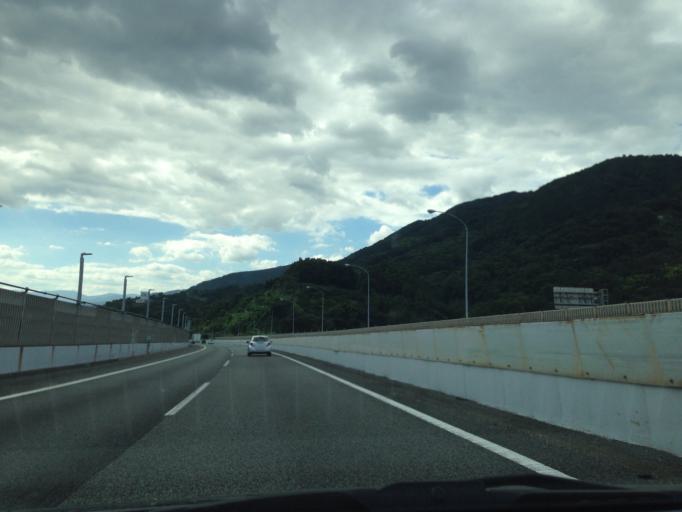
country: JP
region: Kanagawa
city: Hadano
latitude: 35.3470
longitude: 139.1517
